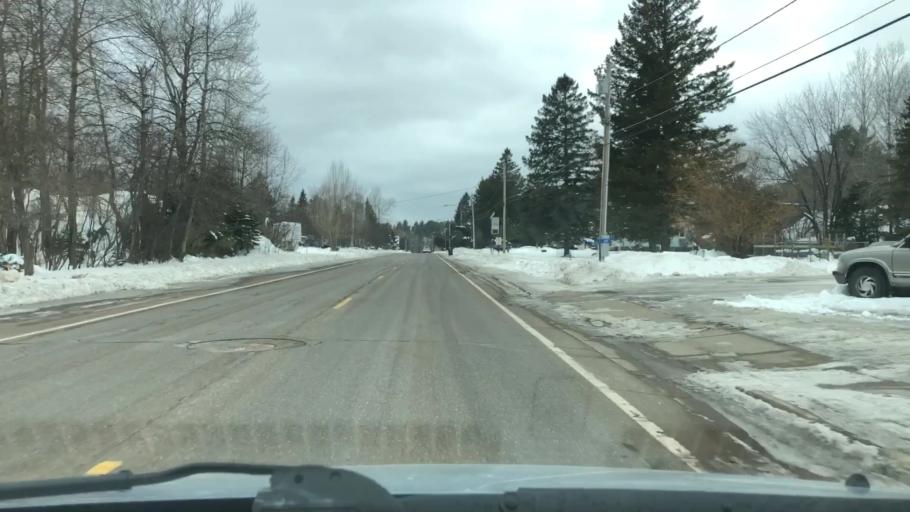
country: US
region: Minnesota
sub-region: Carlton County
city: Carlton
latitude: 46.6636
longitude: -92.3913
